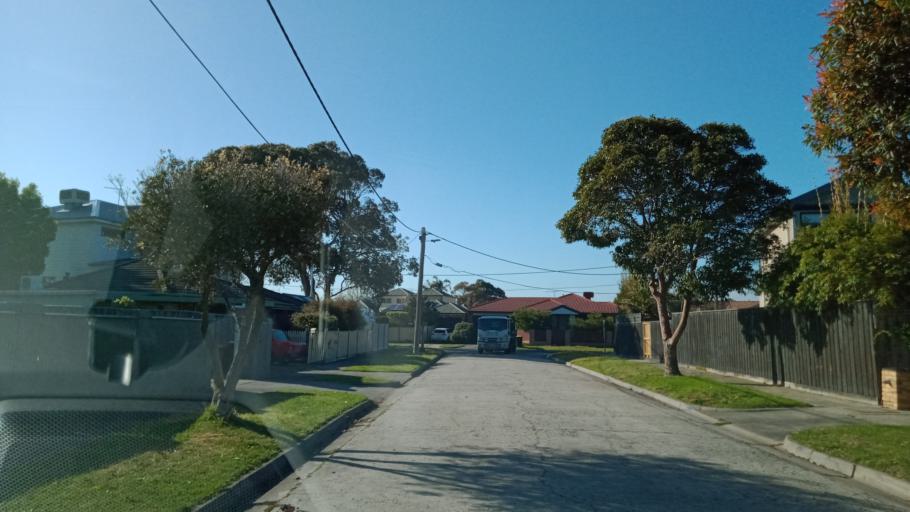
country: AU
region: Victoria
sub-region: Kingston
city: Chelsea
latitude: -38.0446
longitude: 145.1170
